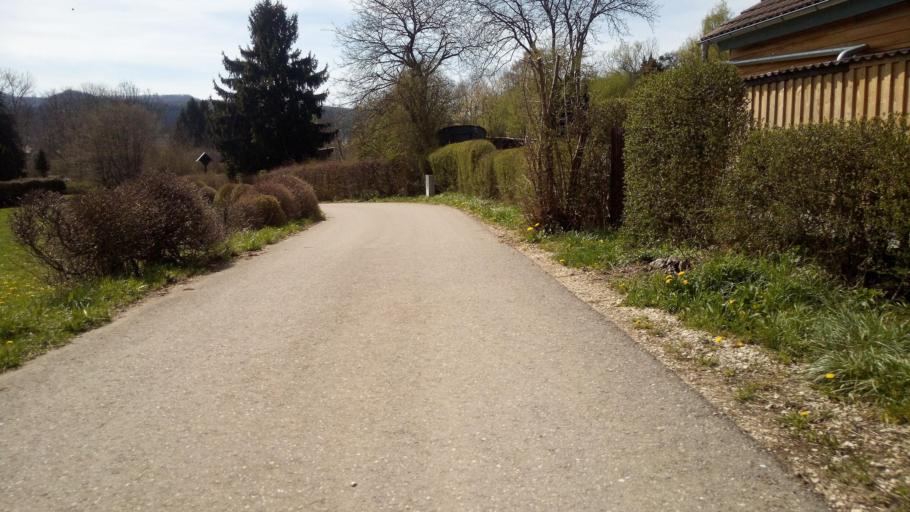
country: DE
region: Baden-Wuerttemberg
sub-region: Regierungsbezirk Stuttgart
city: Donzdorf
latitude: 48.6952
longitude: 9.8137
